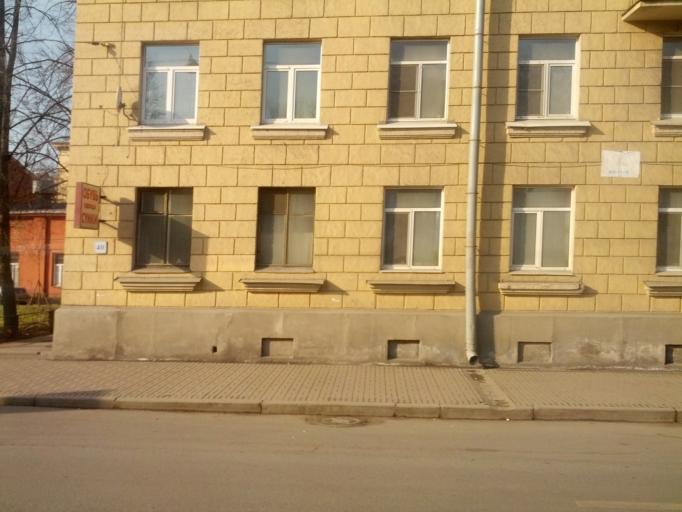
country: RU
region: Leningrad
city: Kalininskiy
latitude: 59.9547
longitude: 30.4152
